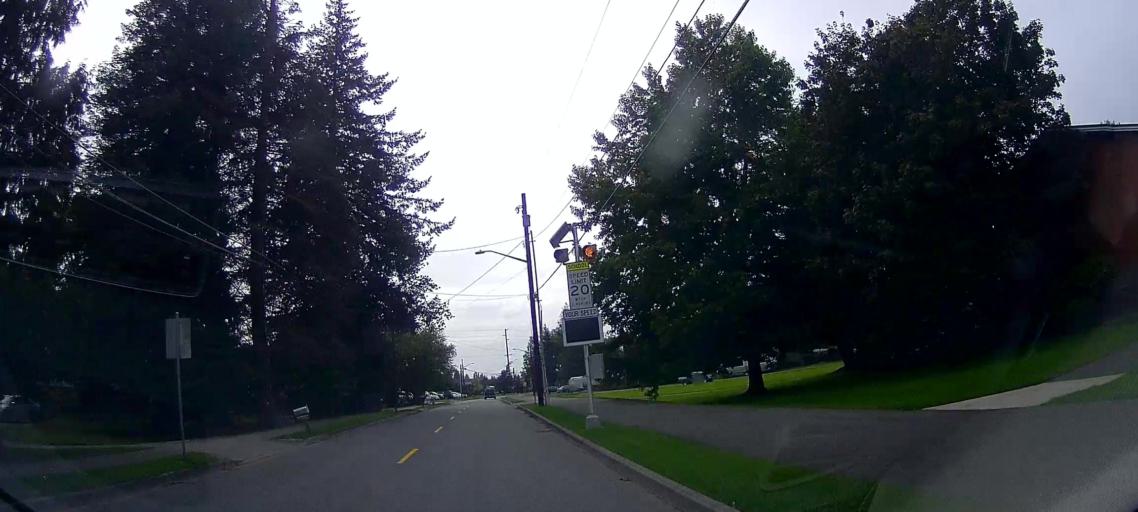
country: US
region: Washington
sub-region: Skagit County
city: Sedro-Woolley
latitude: 48.5154
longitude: -122.2204
